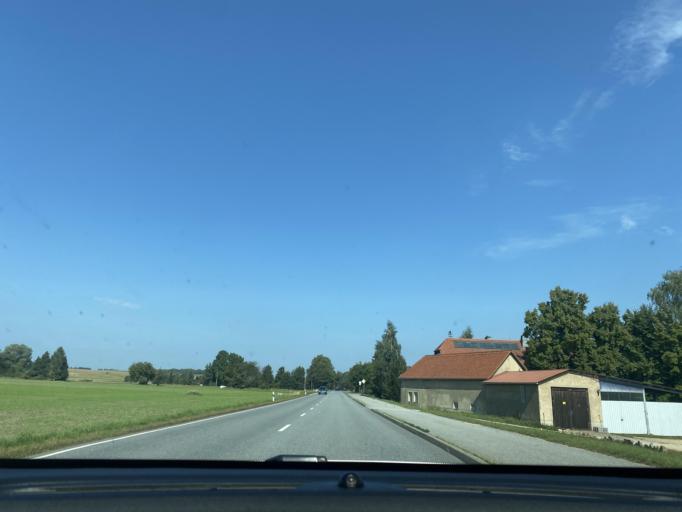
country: DE
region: Saxony
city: Quitzdorf
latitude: 51.2122
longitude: 14.7684
